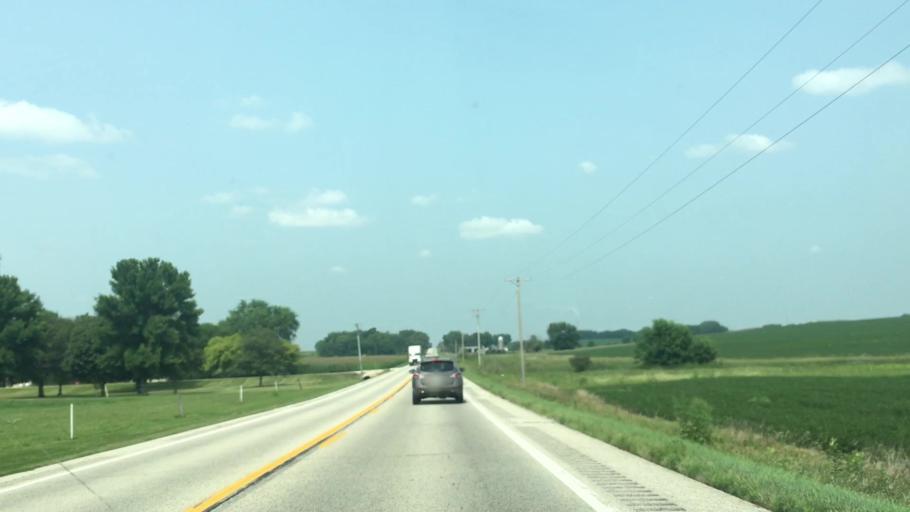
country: US
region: Iowa
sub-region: Buchanan County
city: Independence
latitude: 42.5222
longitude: -91.8898
